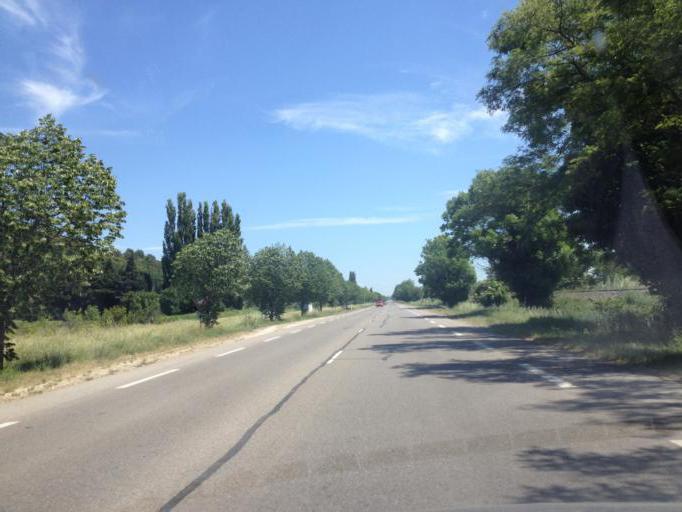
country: FR
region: Provence-Alpes-Cote d'Azur
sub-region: Departement du Vaucluse
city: Lauris
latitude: 43.7440
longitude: 5.3121
